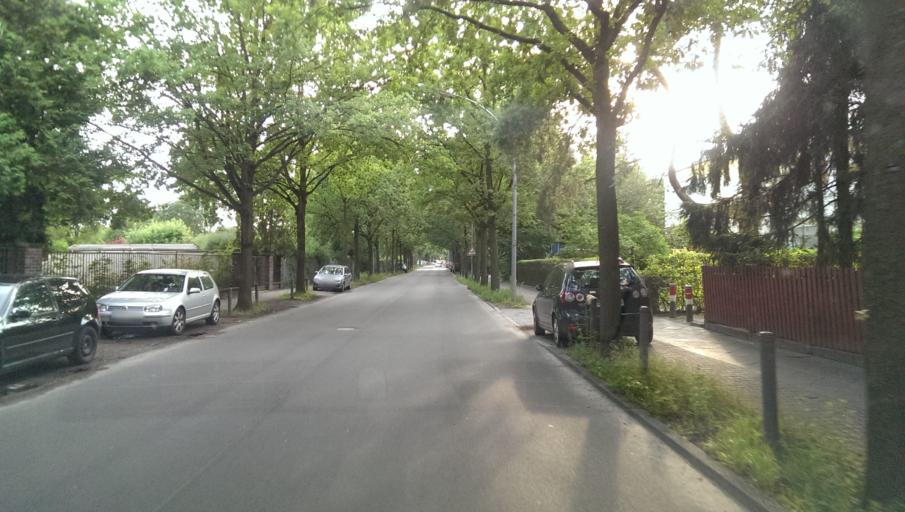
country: DE
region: Berlin
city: Lichterfelde
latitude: 52.4108
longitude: 13.3277
